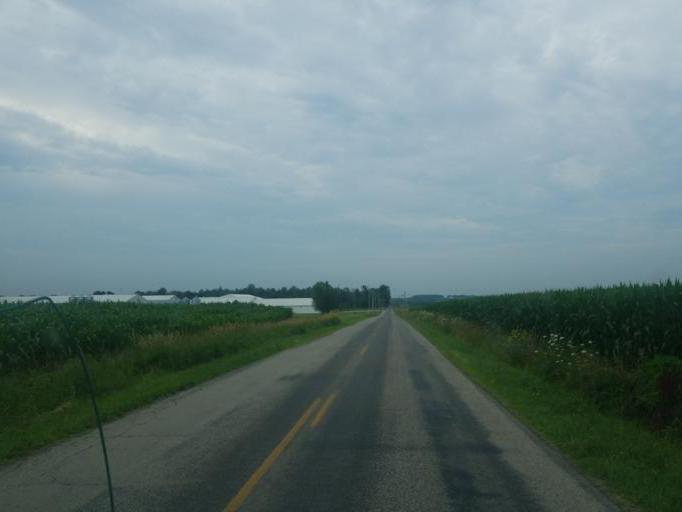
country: US
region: Ohio
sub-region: Wayne County
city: Dalton
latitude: 40.8195
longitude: -81.6480
